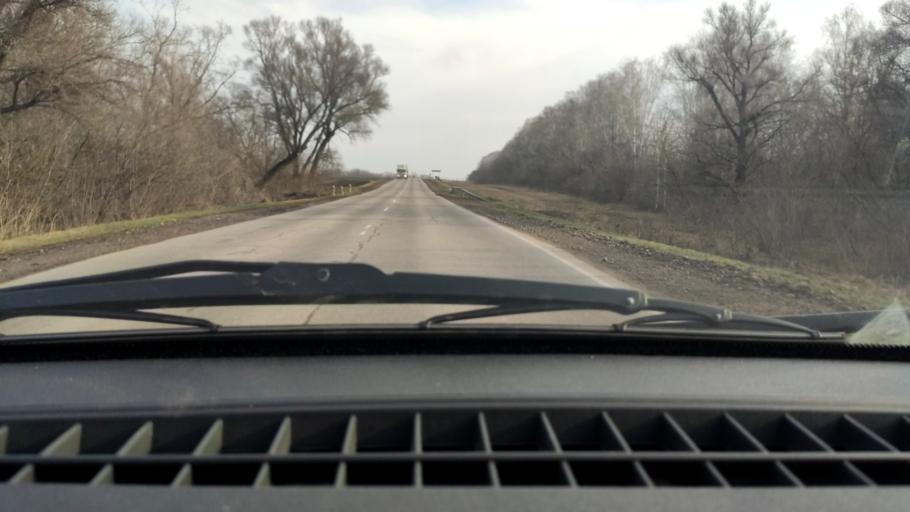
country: RU
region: Bashkortostan
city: Chishmy
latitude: 54.5211
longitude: 55.2982
